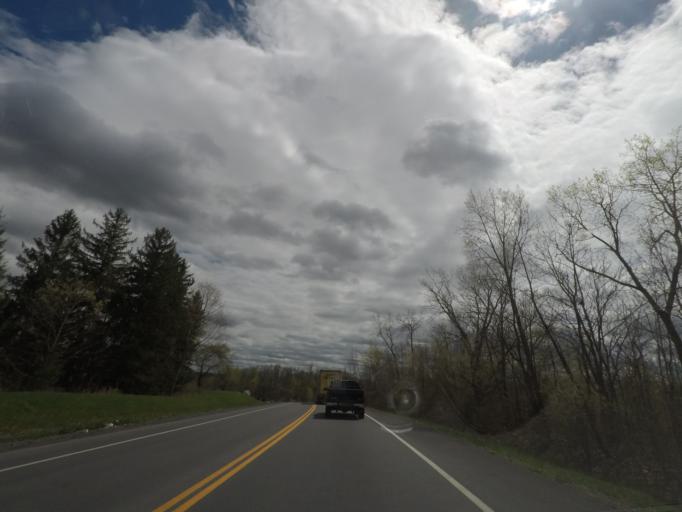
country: US
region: New York
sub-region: Albany County
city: Ravena
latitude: 42.4811
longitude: -73.7940
